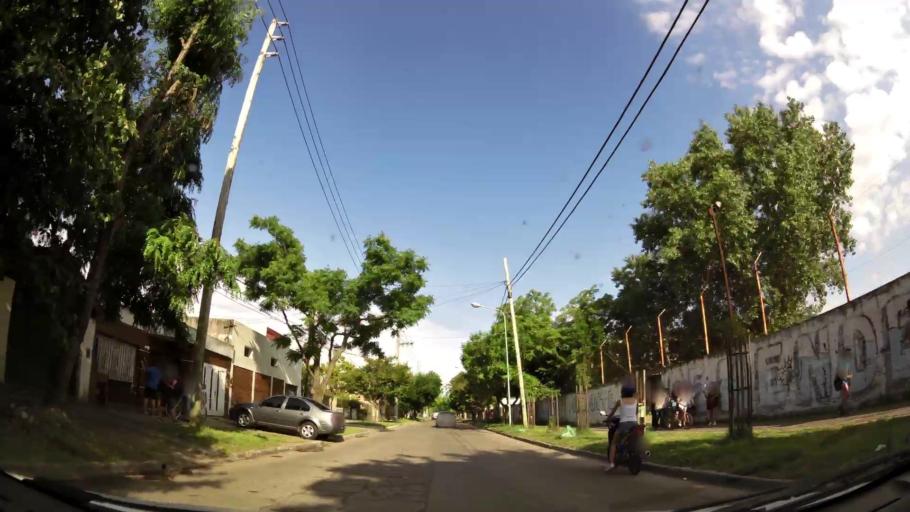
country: AR
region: Buenos Aires
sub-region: Partido de Merlo
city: Merlo
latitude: -34.6618
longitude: -58.7327
